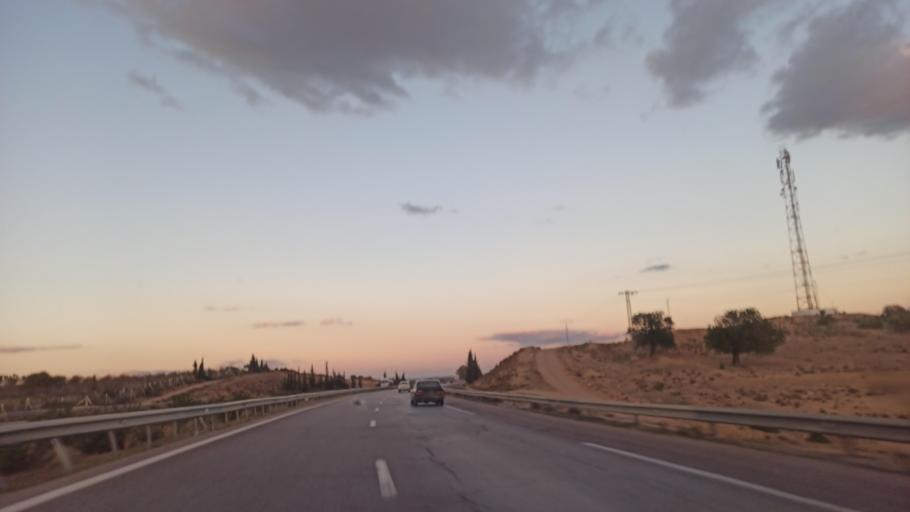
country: TN
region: Susah
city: Harqalah
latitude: 36.2375
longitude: 10.4160
